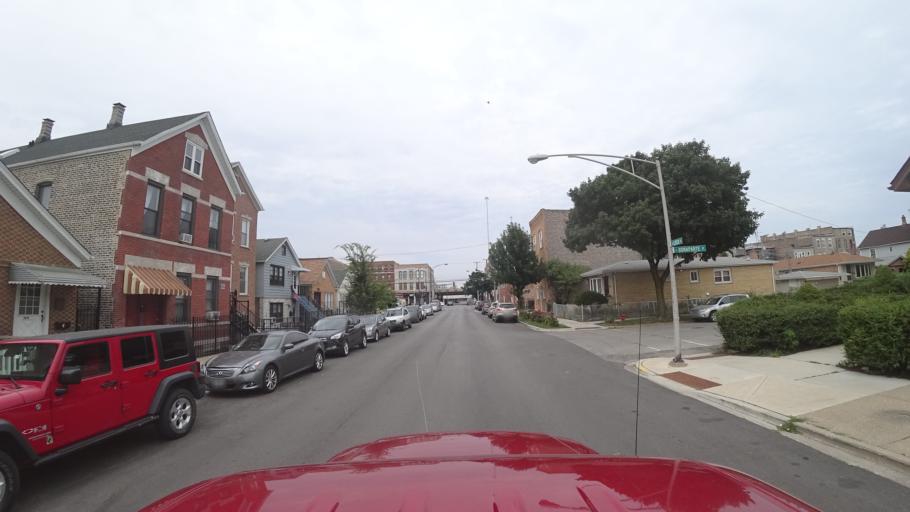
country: US
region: Illinois
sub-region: Cook County
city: Chicago
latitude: 41.8392
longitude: -87.6605
